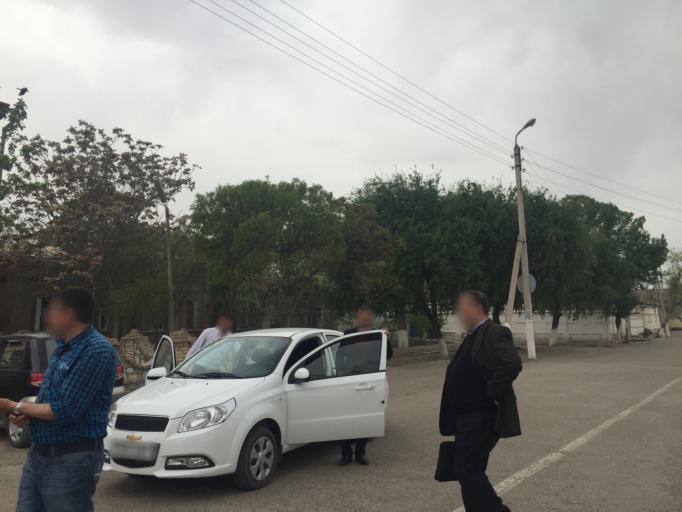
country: UZ
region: Bukhara
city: Kogon
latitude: 39.7197
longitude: 64.5483
